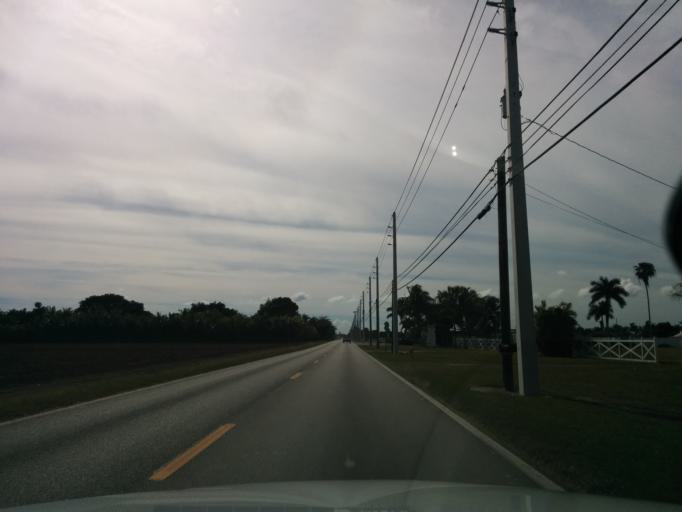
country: US
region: Florida
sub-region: Miami-Dade County
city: Florida City
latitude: 25.4282
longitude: -80.5015
